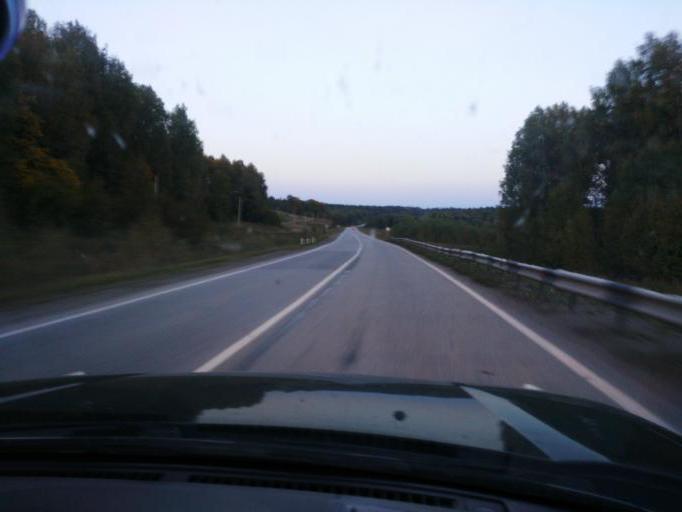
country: RU
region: Perm
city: Verkhnechusovskiye Gorodki
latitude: 58.2819
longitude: 56.9038
